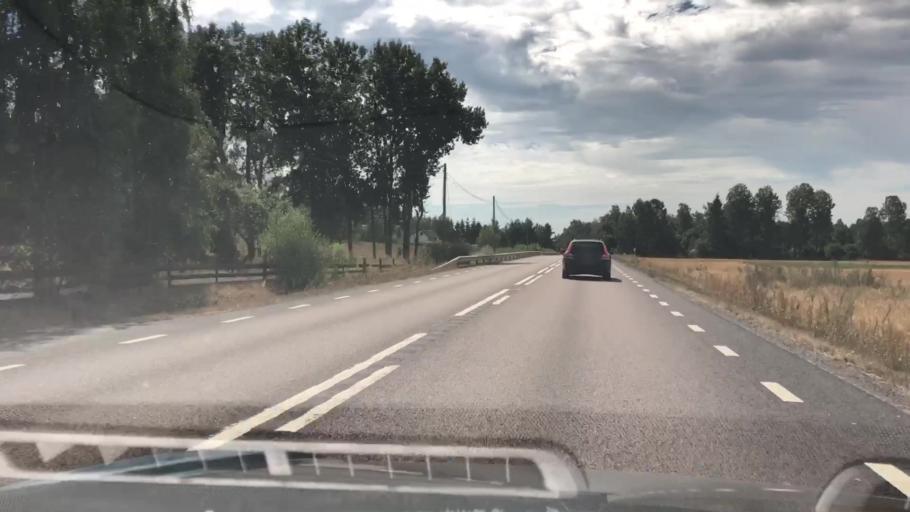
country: SE
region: Kalmar
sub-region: Torsas Kommun
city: Torsas
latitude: 56.3469
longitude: 16.0479
